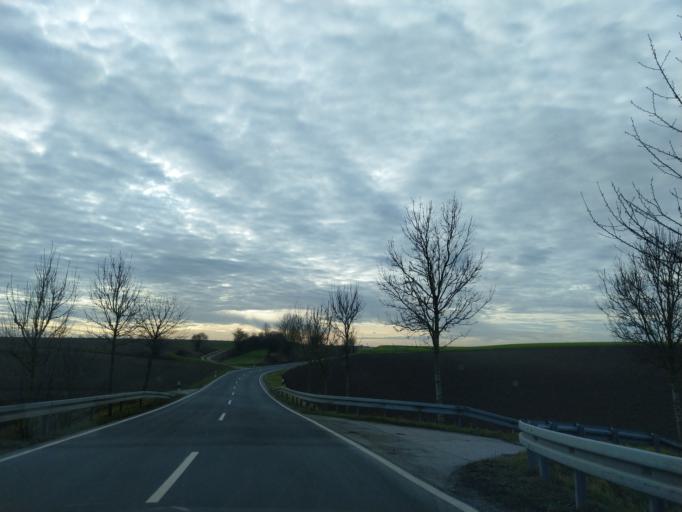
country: DE
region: Bavaria
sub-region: Lower Bavaria
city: Moos
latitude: 48.7370
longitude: 12.9413
